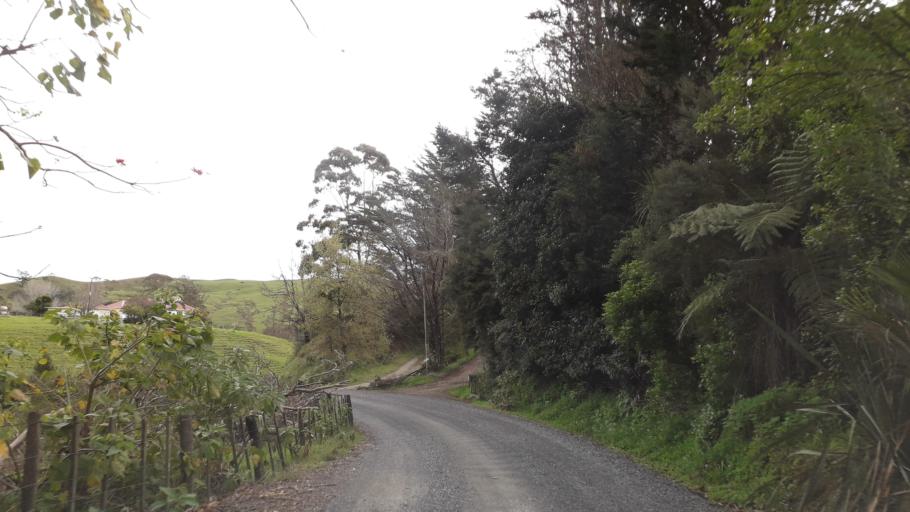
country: NZ
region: Northland
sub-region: Far North District
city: Taipa
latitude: -35.0933
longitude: 173.5222
